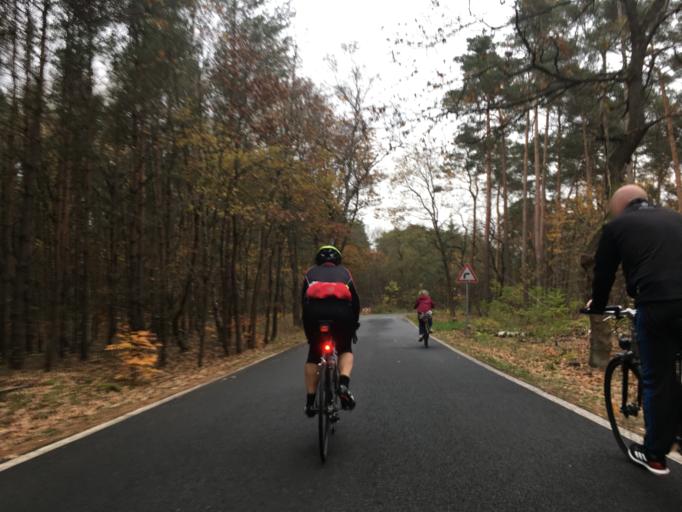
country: DE
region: Brandenburg
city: Gross Lindow
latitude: 52.2758
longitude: 14.4819
